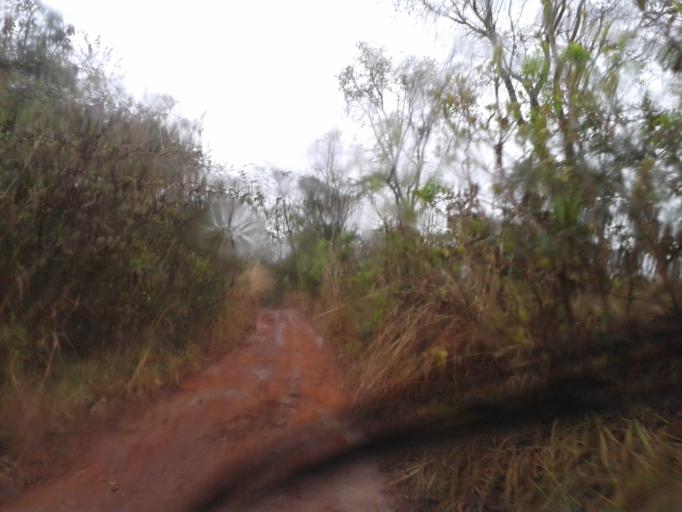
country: BR
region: Minas Gerais
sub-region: Campina Verde
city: Campina Verde
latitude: -19.3459
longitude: -49.5273
